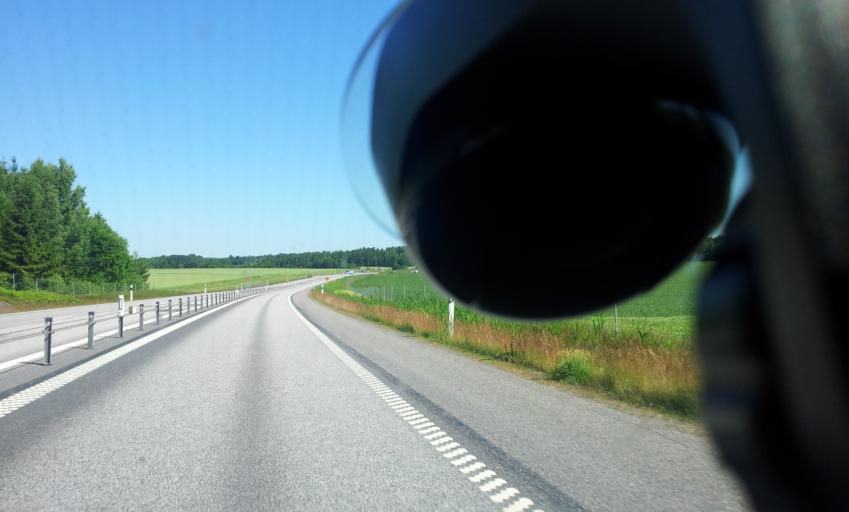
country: SE
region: OEstergoetland
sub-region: Soderkopings Kommun
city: Soederkoeping
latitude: 58.4458
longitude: 16.3668
